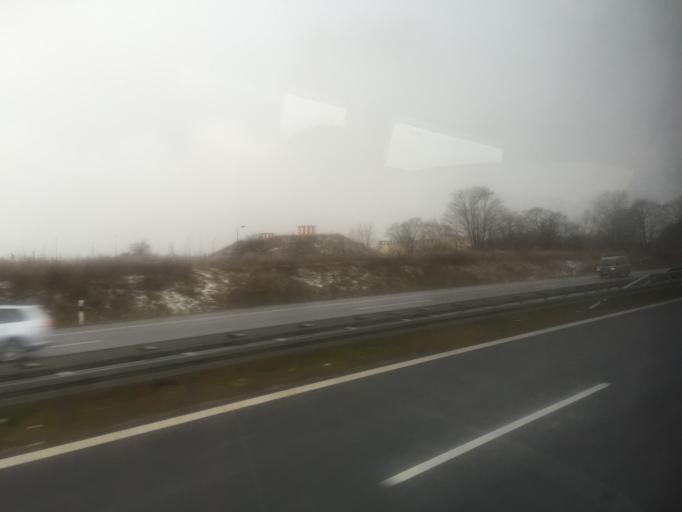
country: DE
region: Brandenburg
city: Schonefeld
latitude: 52.3863
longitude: 13.5318
